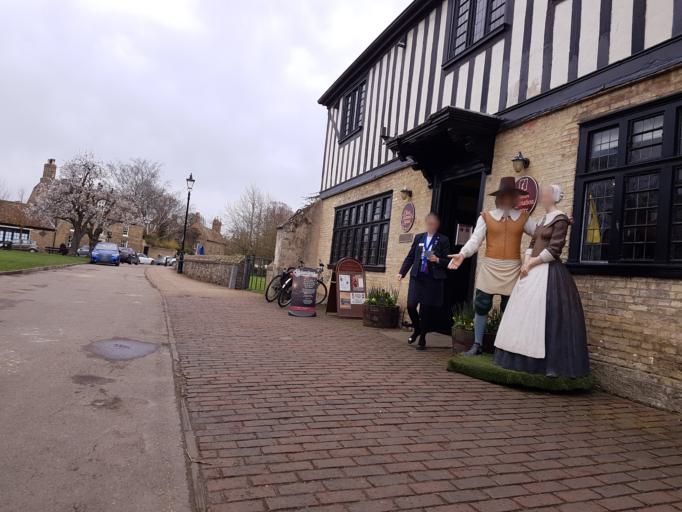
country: GB
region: England
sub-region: Cambridgeshire
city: Ely
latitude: 52.3988
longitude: 0.2591
